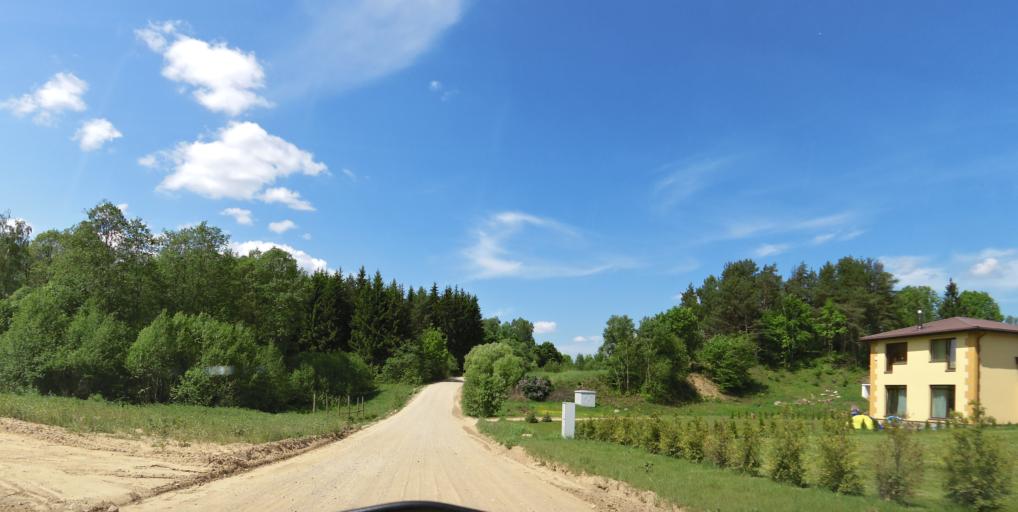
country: LT
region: Vilnius County
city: Pilaite
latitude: 54.7412
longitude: 25.1418
